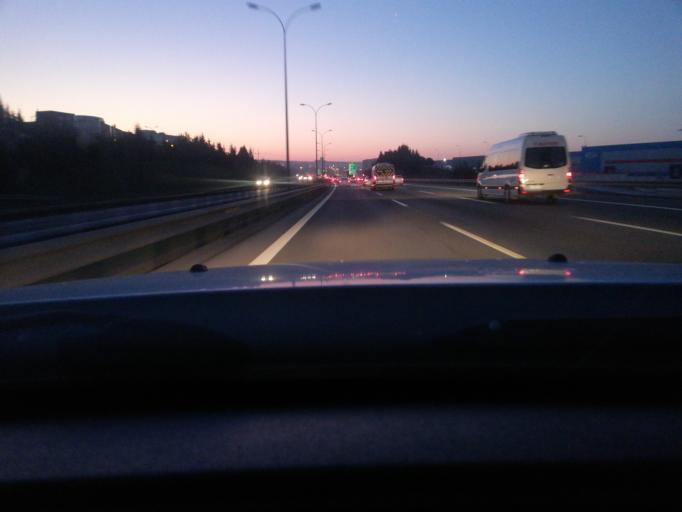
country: TR
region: Kocaeli
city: Balcik
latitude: 40.8798
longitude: 29.3825
